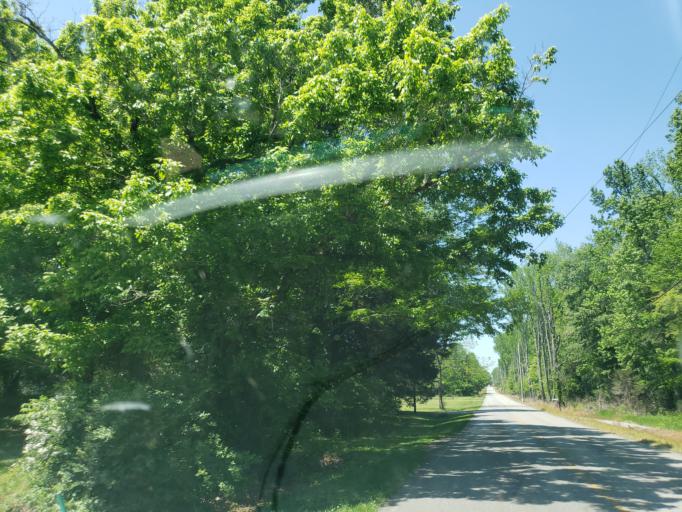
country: US
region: Alabama
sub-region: Madison County
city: Hazel Green
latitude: 34.9616
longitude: -86.5777
